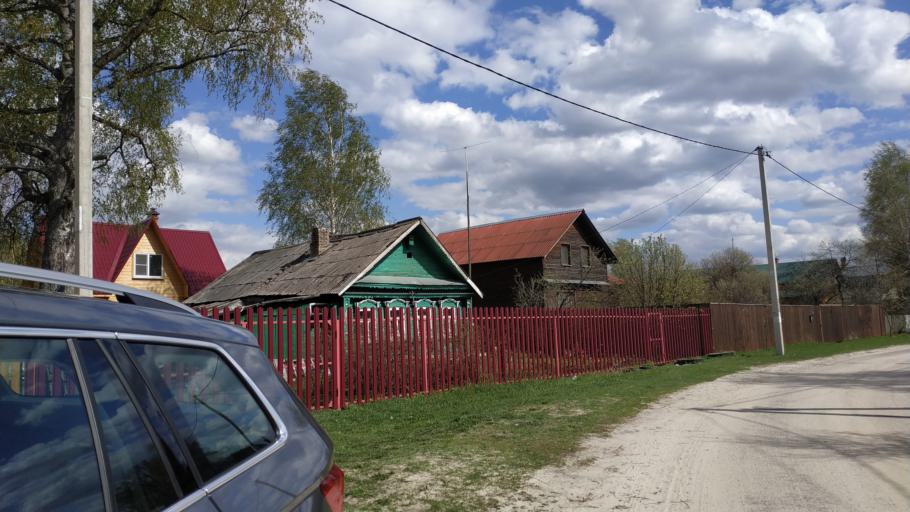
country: RU
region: Moskovskaya
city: Davydovo
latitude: 55.6385
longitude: 38.7796
